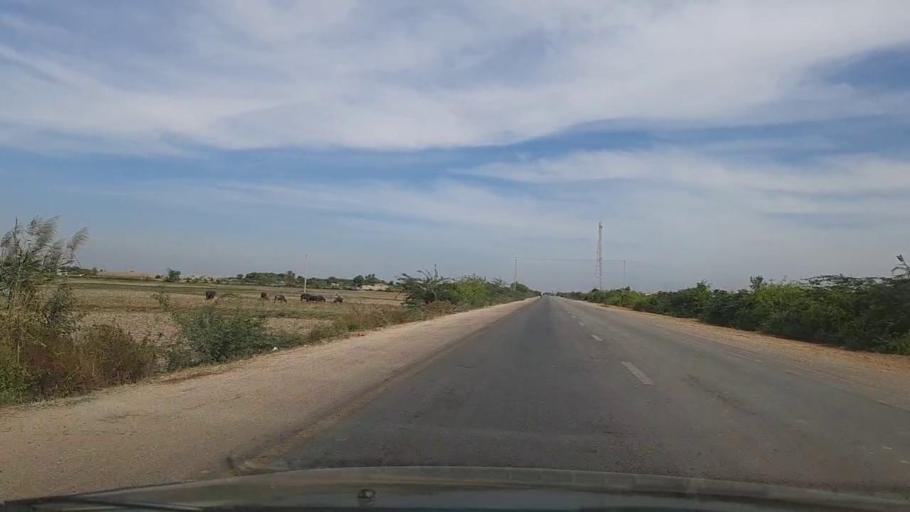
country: PK
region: Sindh
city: Thatta
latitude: 24.8086
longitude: 67.9734
